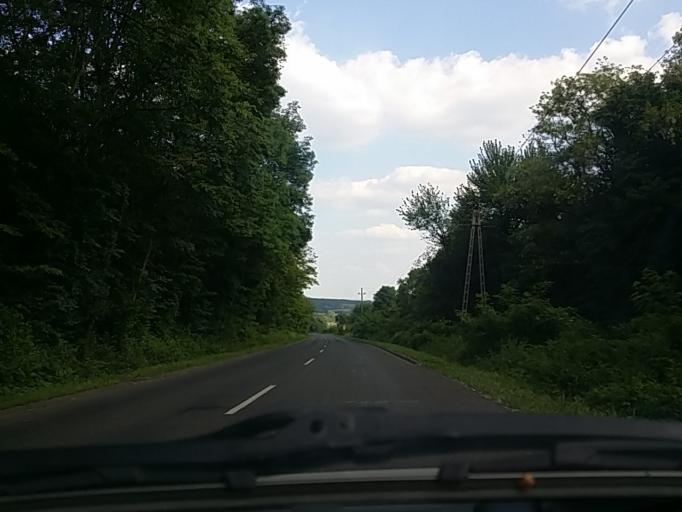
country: HU
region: Pest
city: Pilisszentkereszt
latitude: 47.6870
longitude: 18.9159
